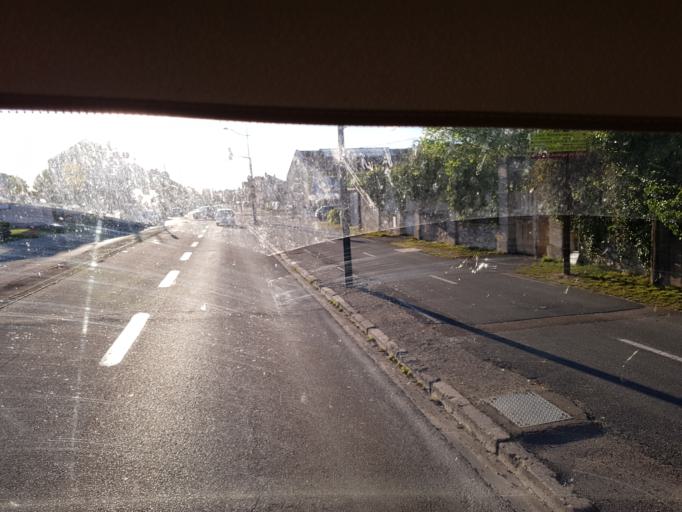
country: FR
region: Champagne-Ardenne
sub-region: Departement de l'Aube
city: Romilly-sur-Seine
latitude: 48.5107
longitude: 3.7256
